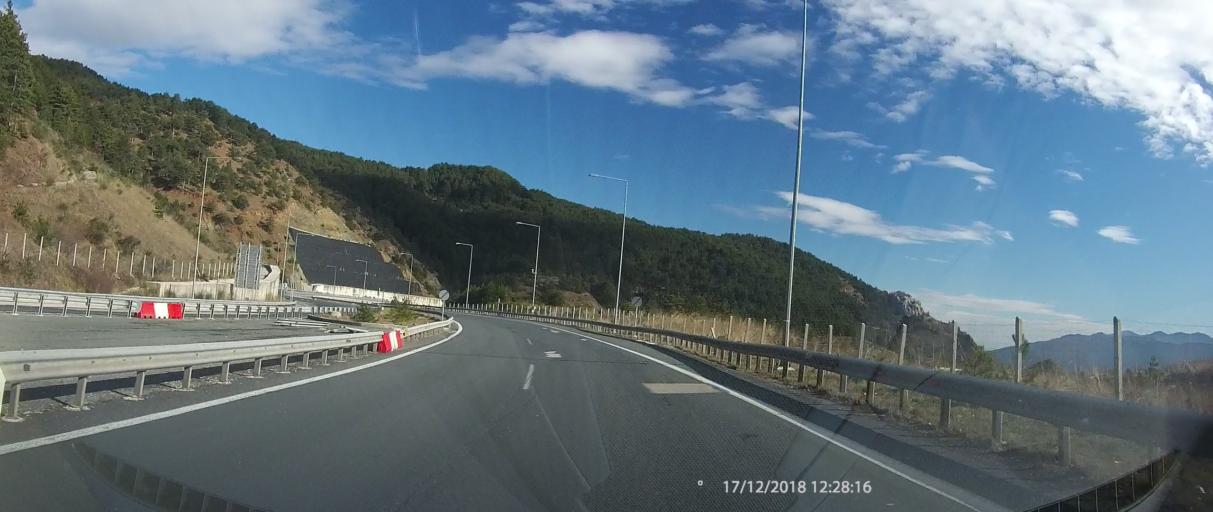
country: GR
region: Epirus
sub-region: Nomos Ioanninon
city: Metsovo
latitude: 39.7890
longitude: 21.2728
